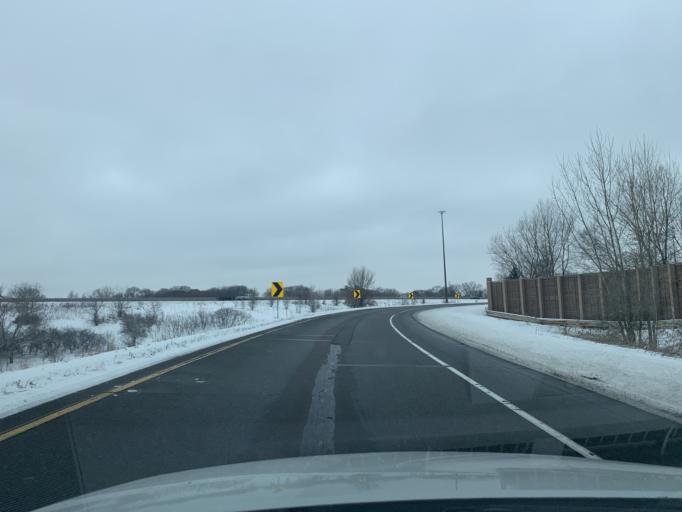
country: US
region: Minnesota
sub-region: Anoka County
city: Coon Rapids
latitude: 45.1442
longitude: -93.2712
